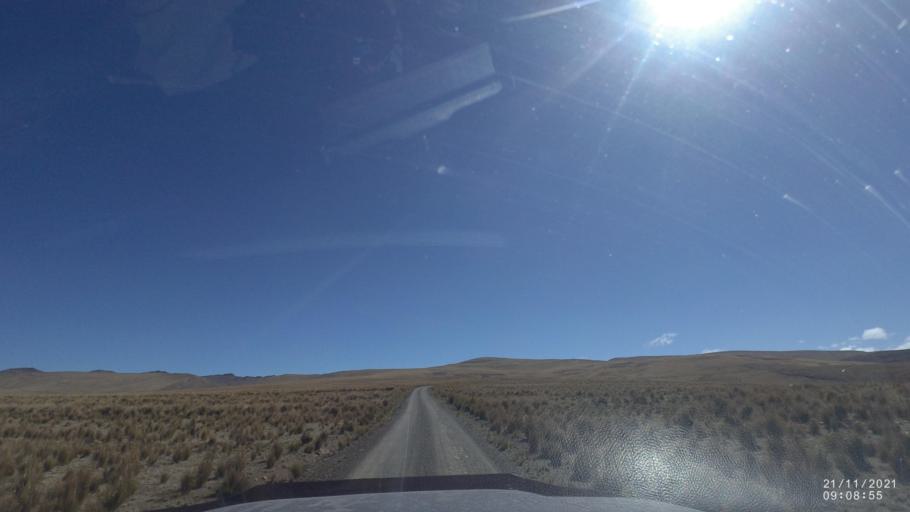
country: BO
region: Cochabamba
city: Cochabamba
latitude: -17.1605
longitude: -66.2649
